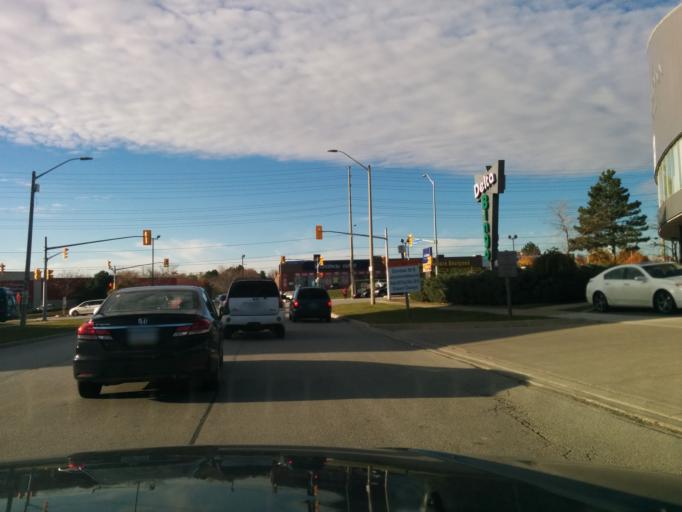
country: CA
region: Ontario
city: Etobicoke
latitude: 43.6140
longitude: -79.5776
